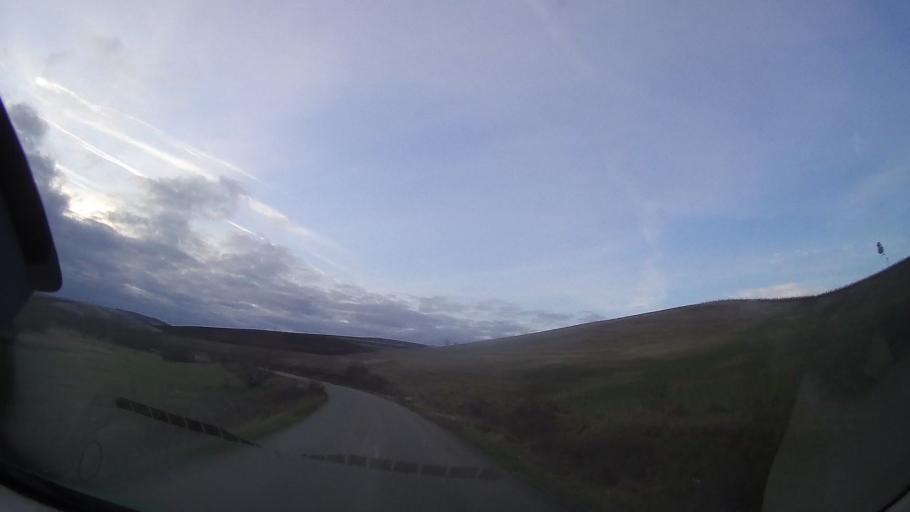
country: RO
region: Cluj
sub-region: Comuna Geaca
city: Geaca
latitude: 46.8533
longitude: 24.0702
